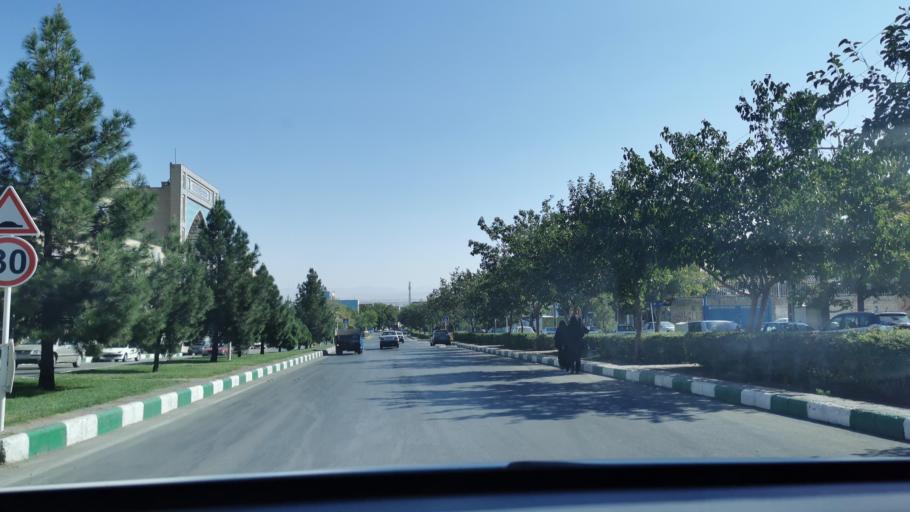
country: IR
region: Razavi Khorasan
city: Mashhad
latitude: 36.3422
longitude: 59.6314
